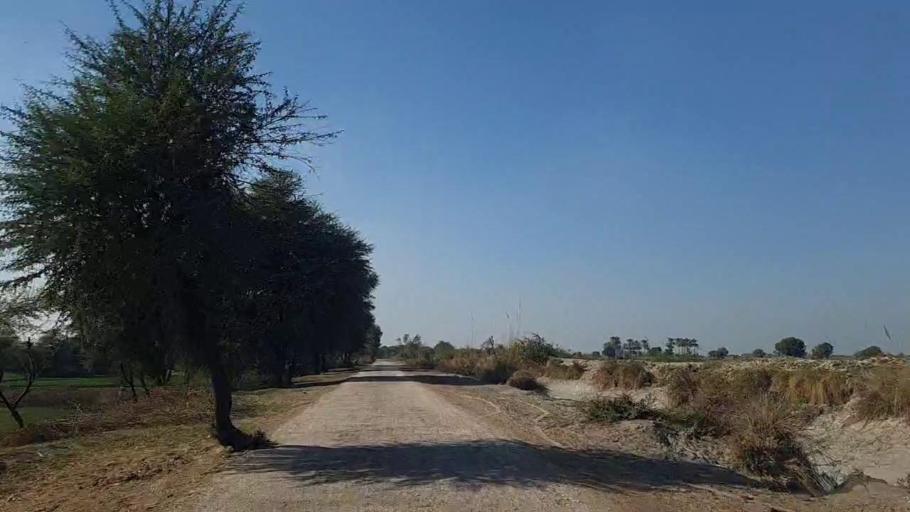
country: PK
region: Sindh
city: Shahpur Chakar
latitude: 26.2129
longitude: 68.6122
